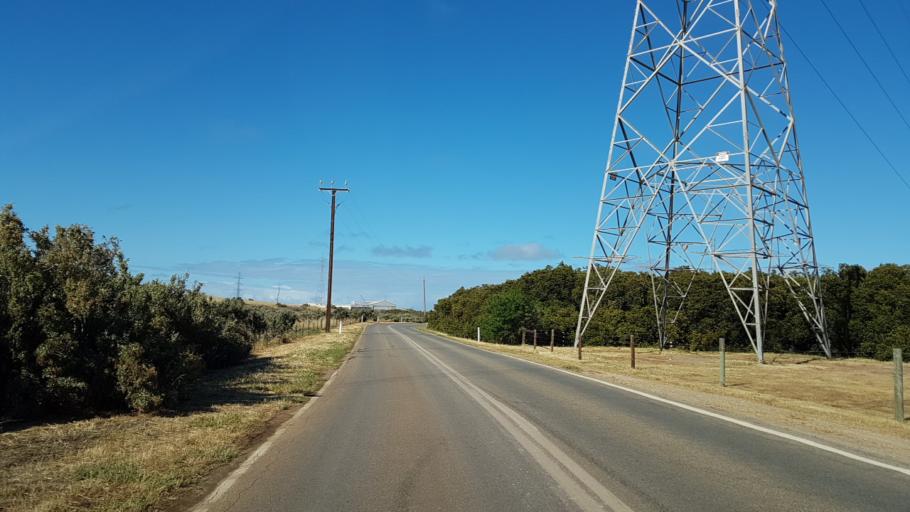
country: AU
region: South Australia
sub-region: Port Adelaide Enfield
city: Birkenhead
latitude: -34.8080
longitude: 138.5288
